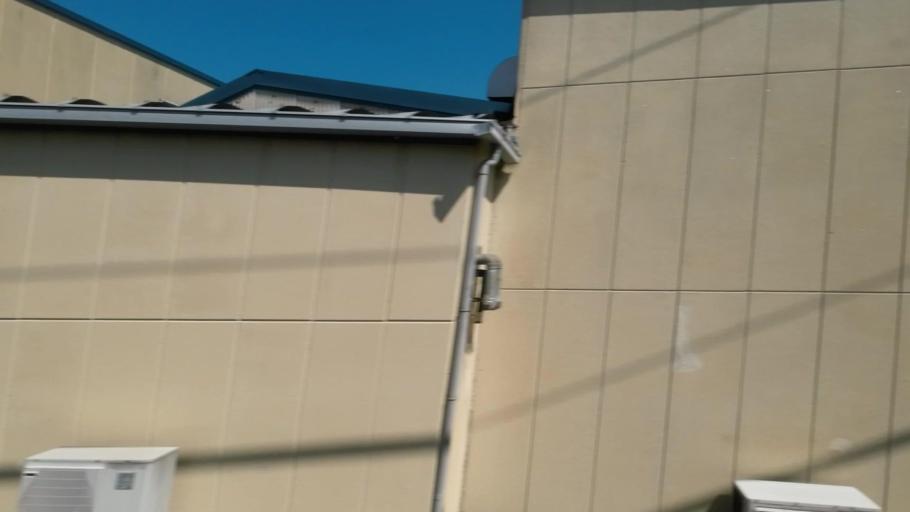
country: JP
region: Ehime
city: Kawanoecho
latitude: 33.9669
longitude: 133.4565
